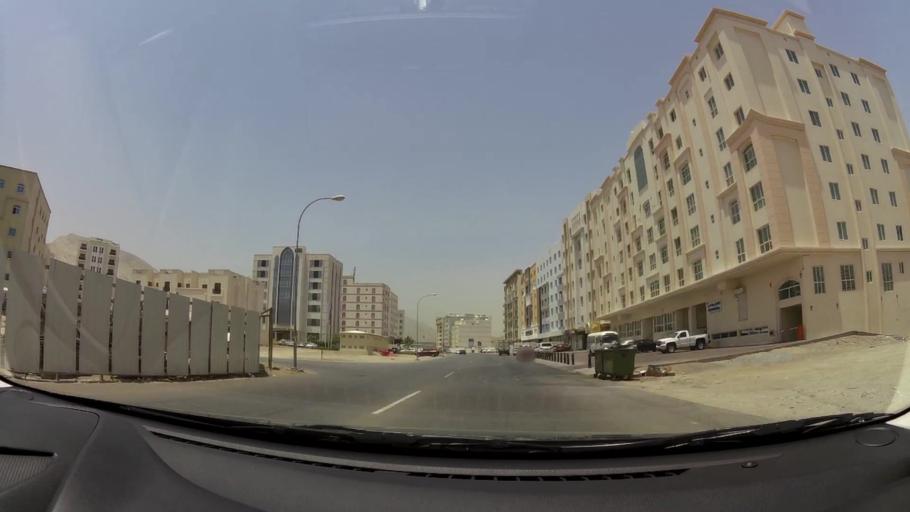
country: OM
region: Muhafazat Masqat
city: Bawshar
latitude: 23.5760
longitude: 58.4175
